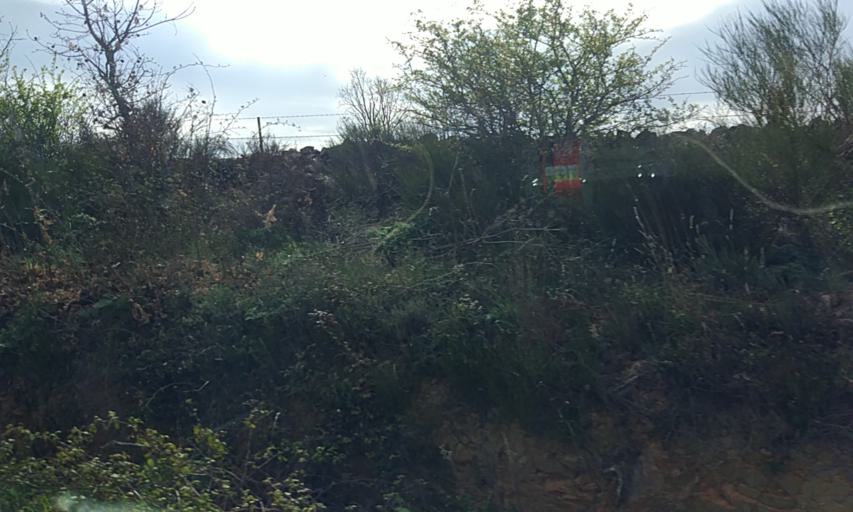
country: ES
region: Castille and Leon
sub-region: Provincia de Salamanca
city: Robleda
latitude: 40.4222
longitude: -6.6012
